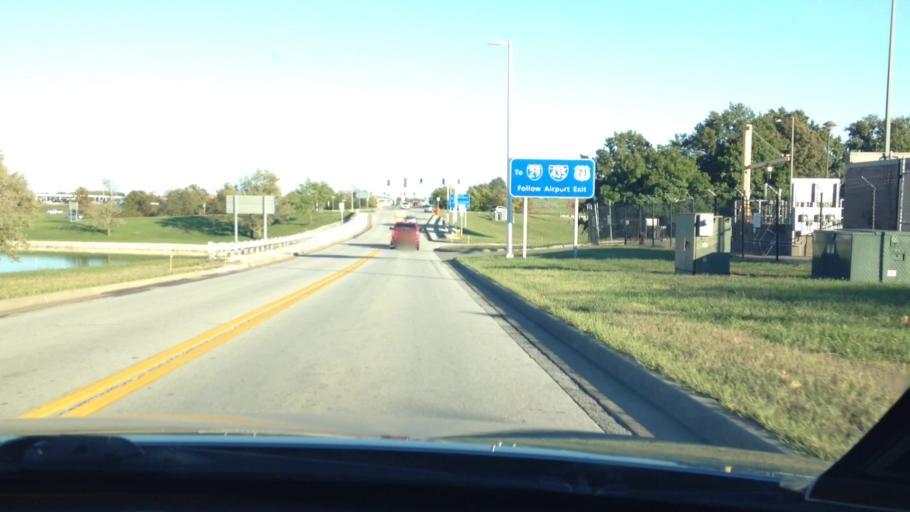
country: US
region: Missouri
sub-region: Platte County
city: Weatherby Lake
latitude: 39.3030
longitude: -94.7169
